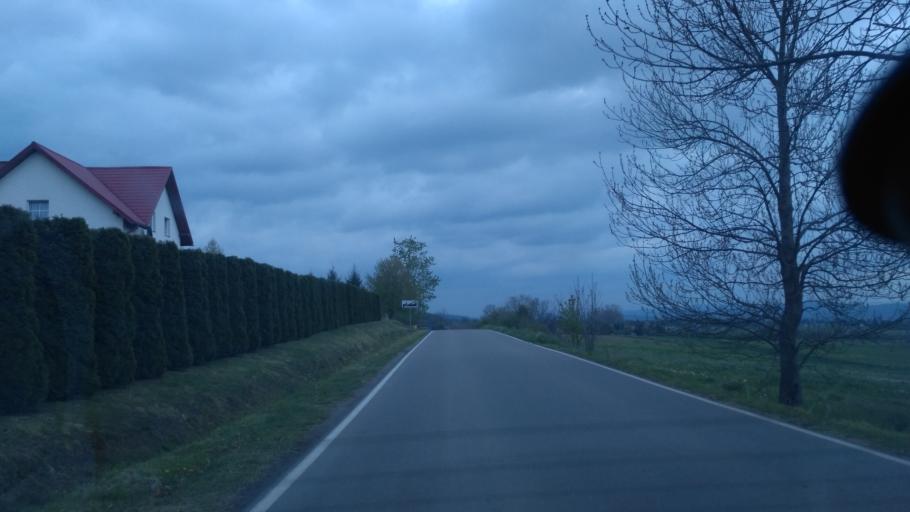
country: PL
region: Subcarpathian Voivodeship
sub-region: Powiat brzozowski
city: Turze Pole
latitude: 49.6390
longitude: 22.0010
